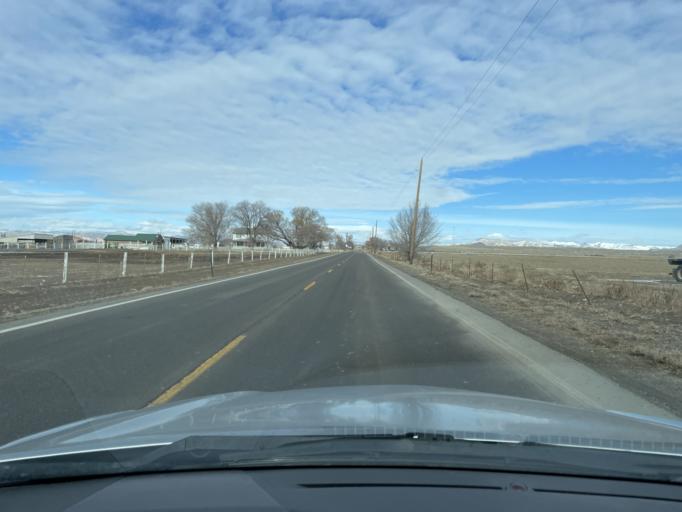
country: US
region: Colorado
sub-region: Mesa County
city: Loma
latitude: 39.2479
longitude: -108.8129
